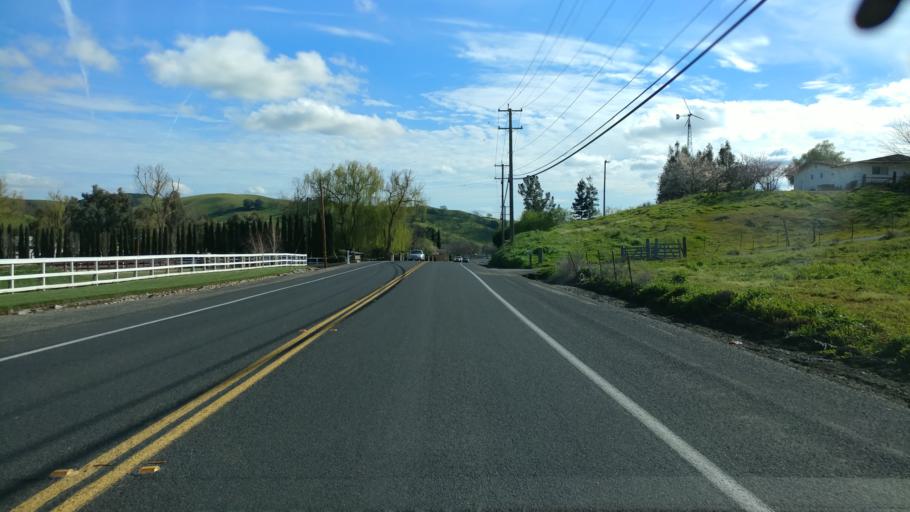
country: US
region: California
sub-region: Contra Costa County
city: Blackhawk
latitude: 37.7835
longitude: -121.8630
